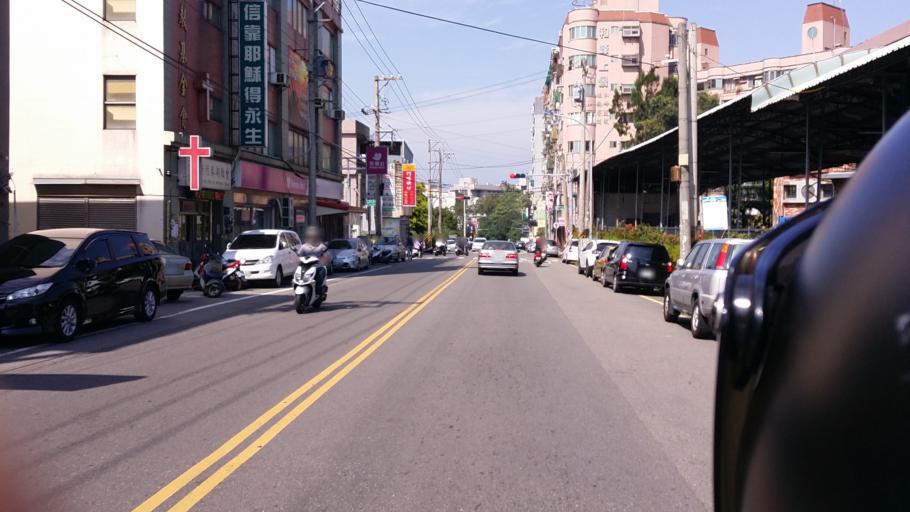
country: TW
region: Taiwan
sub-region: Hsinchu
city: Hsinchu
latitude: 24.7901
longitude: 120.9654
